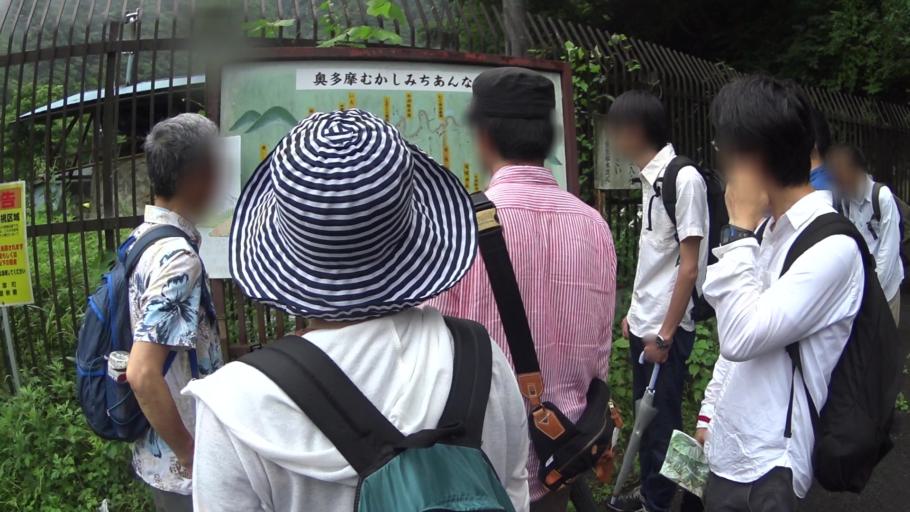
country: JP
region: Tokyo
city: Itsukaichi
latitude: 35.7898
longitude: 139.0557
